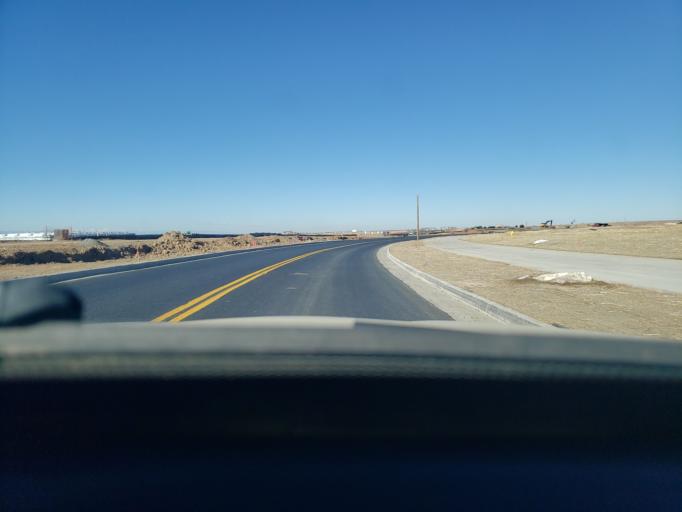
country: US
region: Colorado
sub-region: Adams County
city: Aurora
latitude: 39.7570
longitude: -104.7133
